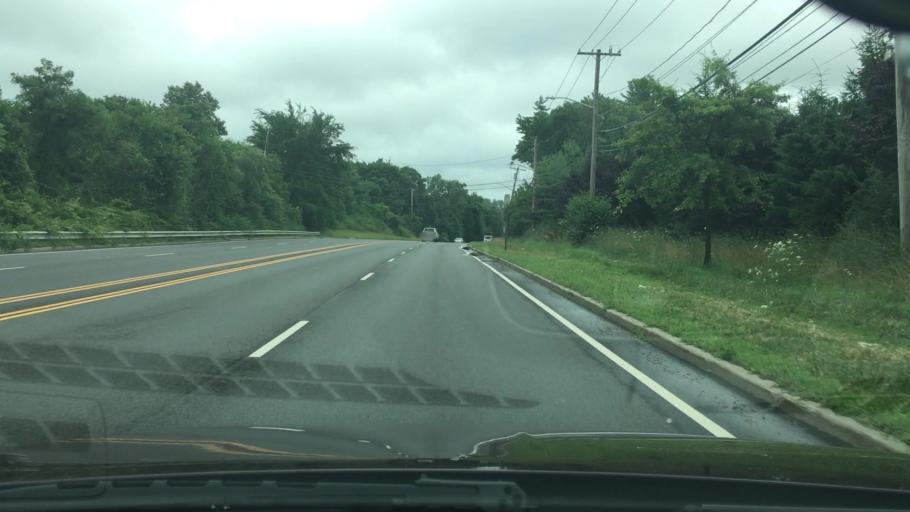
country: US
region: New York
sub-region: Nassau County
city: Jericho
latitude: 40.8005
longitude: -73.5310
